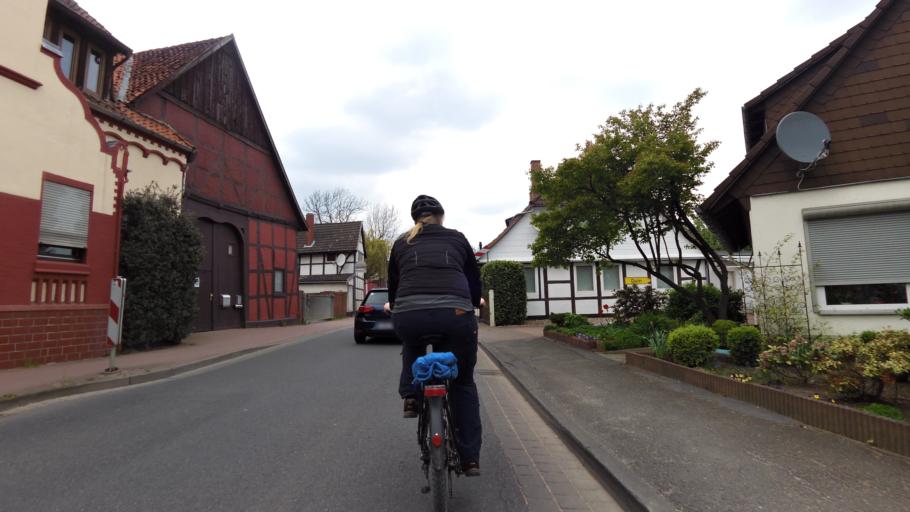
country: DE
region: Lower Saxony
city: Hemmingen
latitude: 52.3215
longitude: 9.7478
